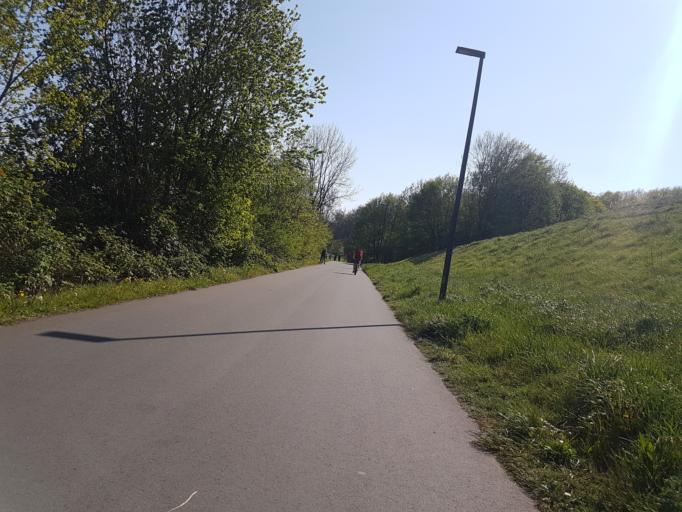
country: DE
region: North Rhine-Westphalia
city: Hattingen
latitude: 51.4182
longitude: 7.2544
